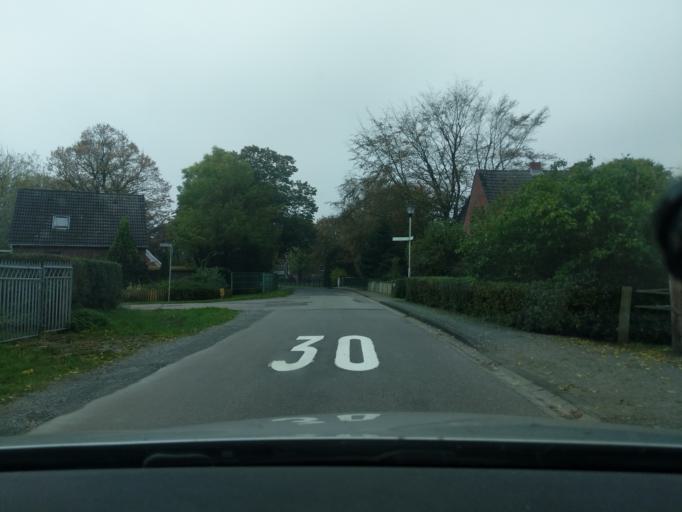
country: DE
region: Lower Saxony
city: Cuxhaven
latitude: 53.8389
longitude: 8.7355
